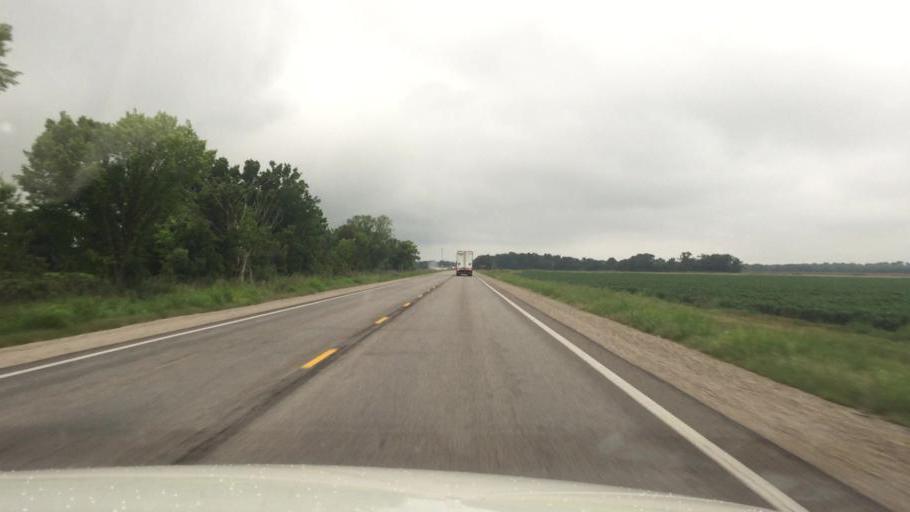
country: US
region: Kansas
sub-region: Montgomery County
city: Coffeyville
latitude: 37.1253
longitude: -95.5808
